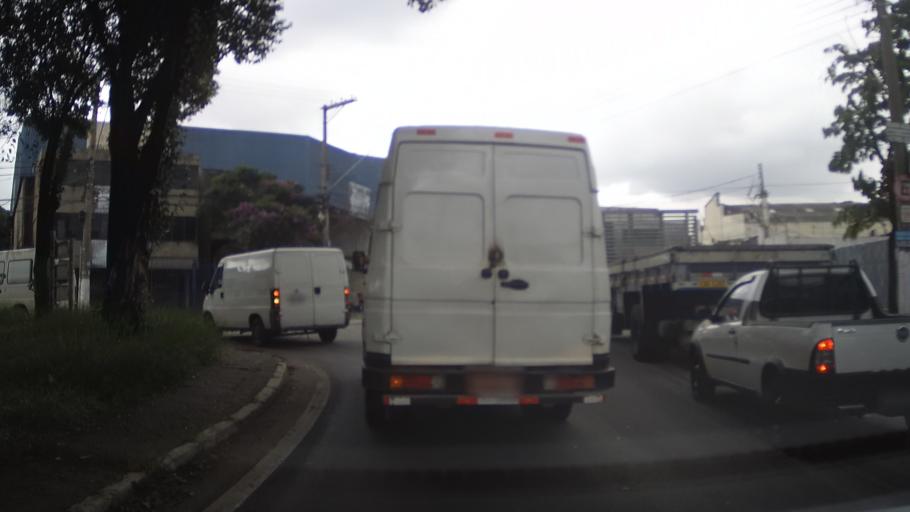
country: BR
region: Sao Paulo
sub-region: Guarulhos
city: Guarulhos
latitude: -23.4621
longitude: -46.4811
